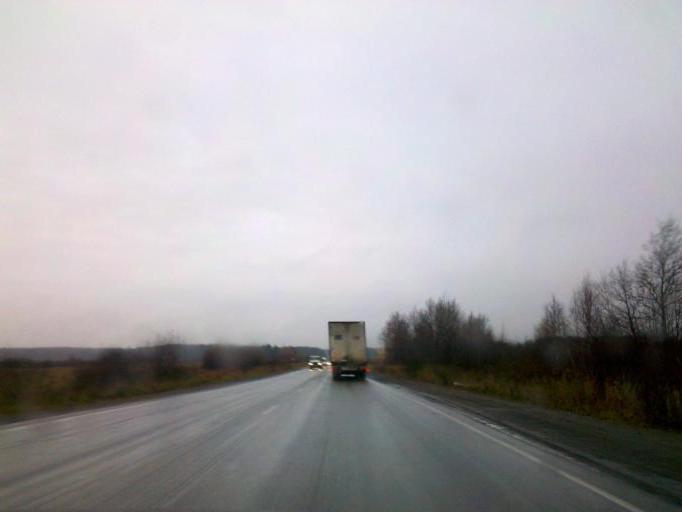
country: RU
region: Republic of Karelia
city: Shuya
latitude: 61.8316
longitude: 34.2085
